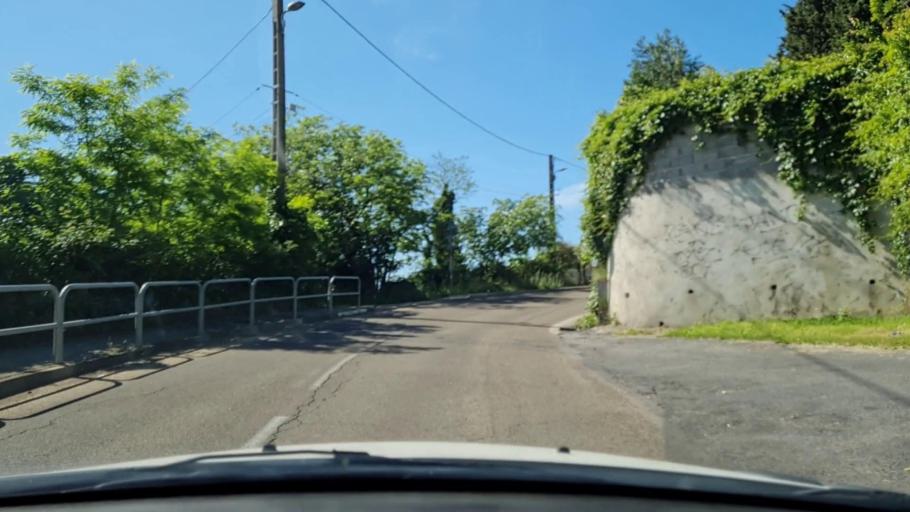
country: FR
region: Languedoc-Roussillon
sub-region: Departement du Gard
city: Cendras
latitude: 44.1425
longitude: 4.0749
